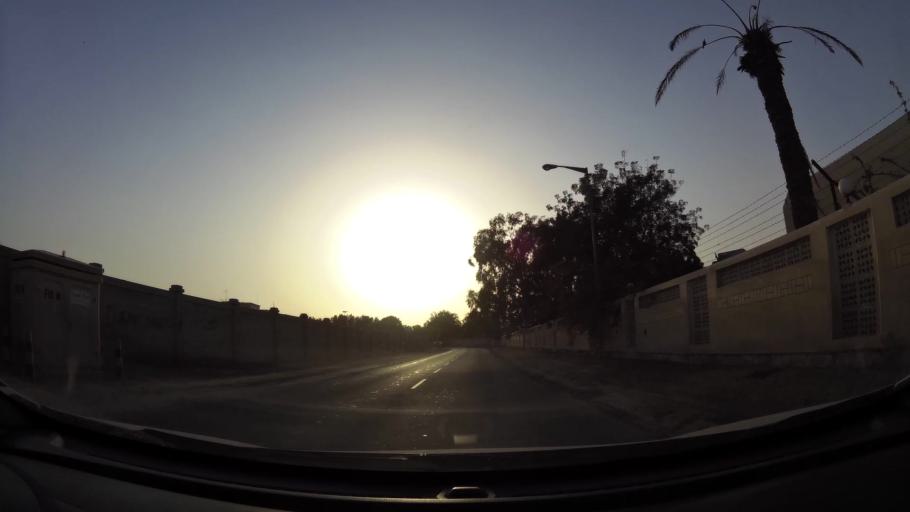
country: BH
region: Manama
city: Jidd Hafs
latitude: 26.2018
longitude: 50.4918
